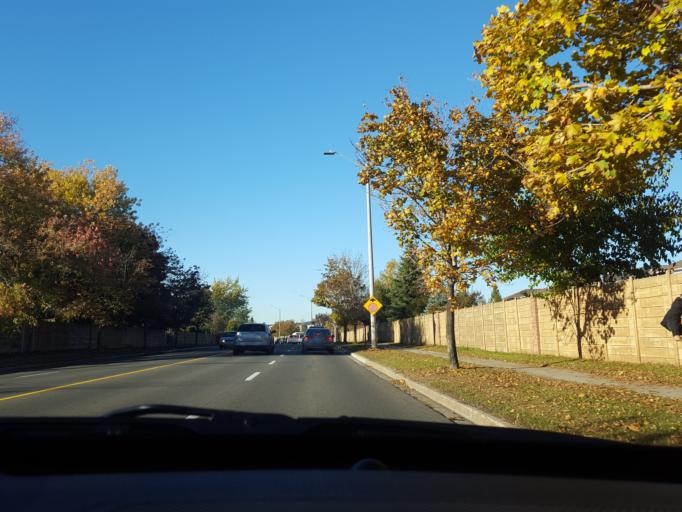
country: CA
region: Ontario
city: Markham
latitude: 43.8380
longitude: -79.2900
